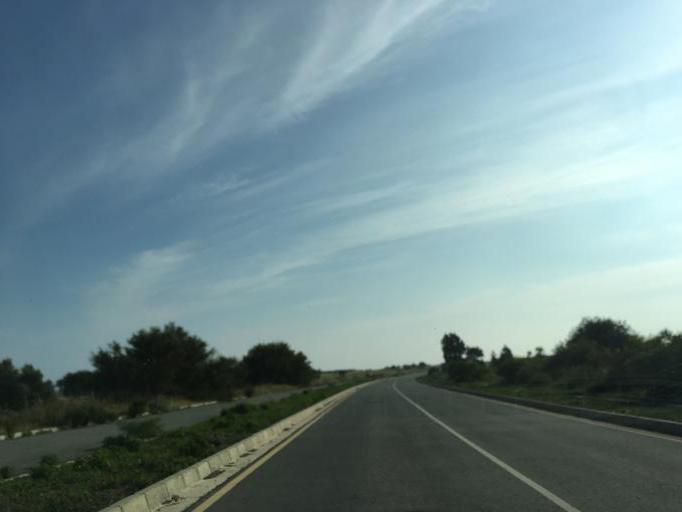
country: CY
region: Larnaka
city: Tersefanou
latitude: 34.7976
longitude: 33.5157
